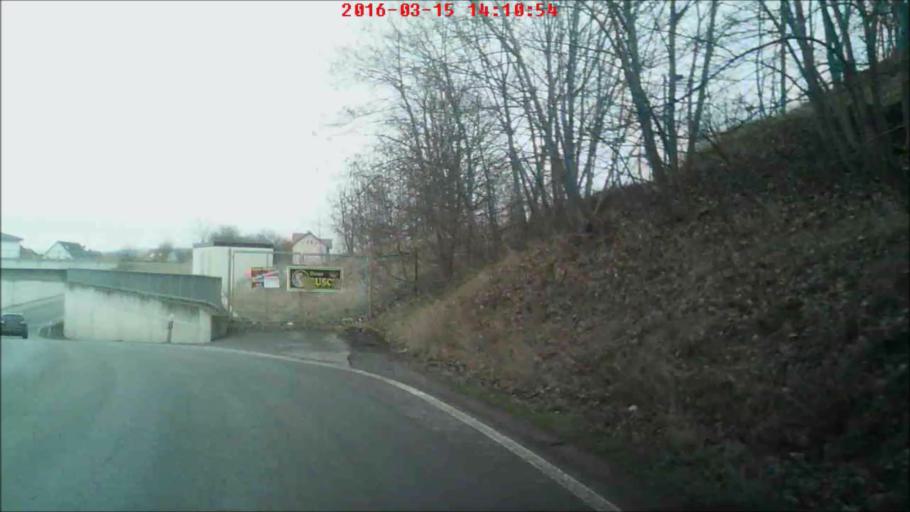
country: DE
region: Thuringia
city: Arnstadt
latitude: 50.8496
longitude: 10.9420
